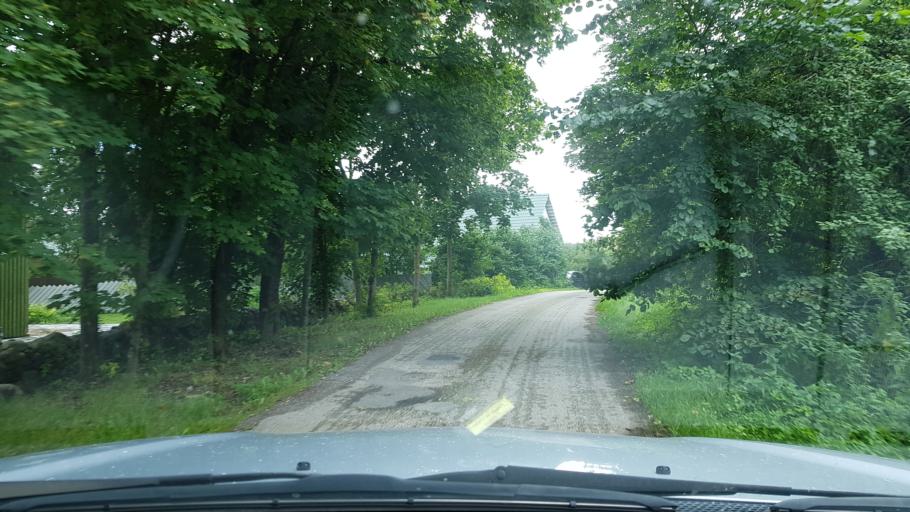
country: EE
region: Harju
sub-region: Rae vald
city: Jueri
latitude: 59.3595
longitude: 24.9508
